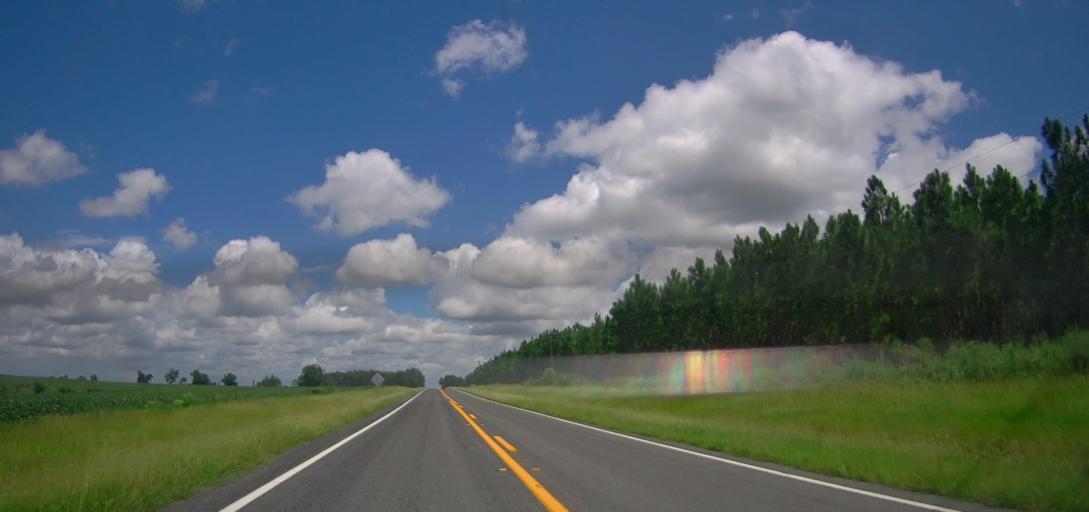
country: US
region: Georgia
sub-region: Turner County
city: Ashburn
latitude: 31.7752
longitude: -83.6151
